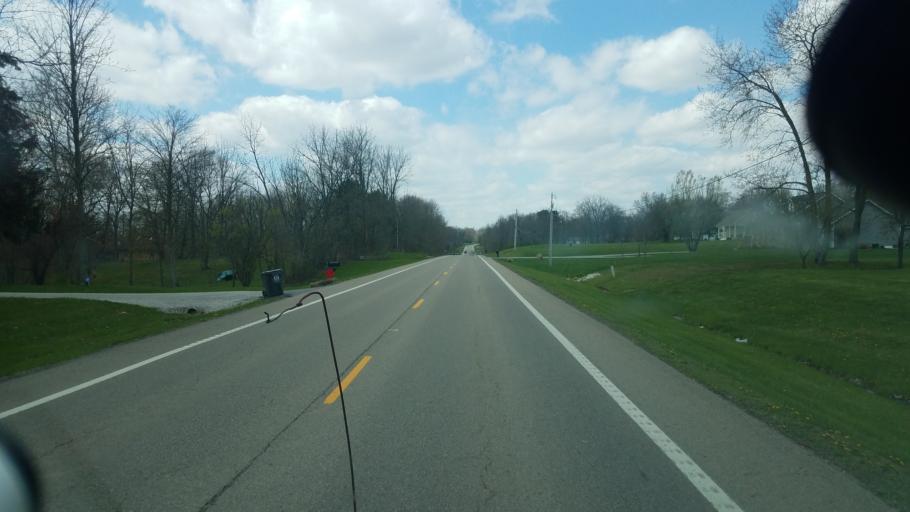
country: US
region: Ohio
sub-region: Licking County
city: Johnstown
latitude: 40.1124
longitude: -82.6471
